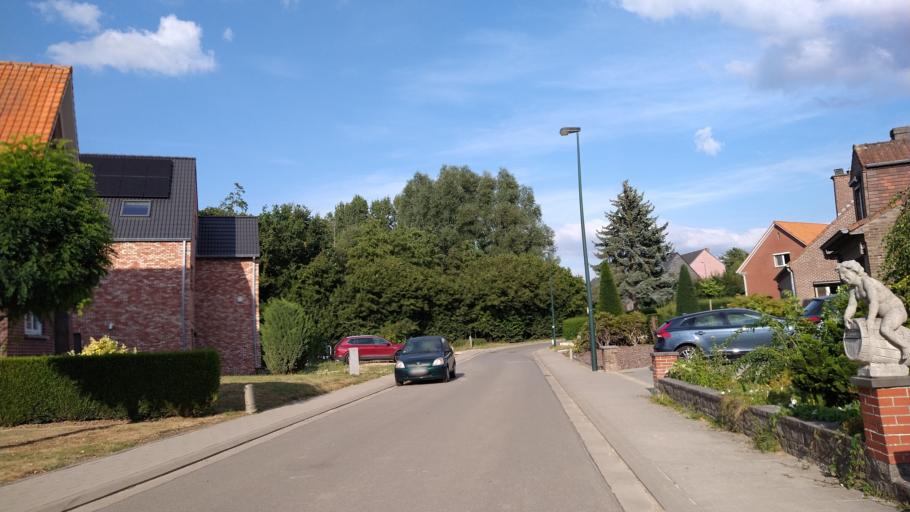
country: BE
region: Flanders
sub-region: Provincie Vlaams-Brabant
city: Tervuren
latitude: 50.8317
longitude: 4.5544
